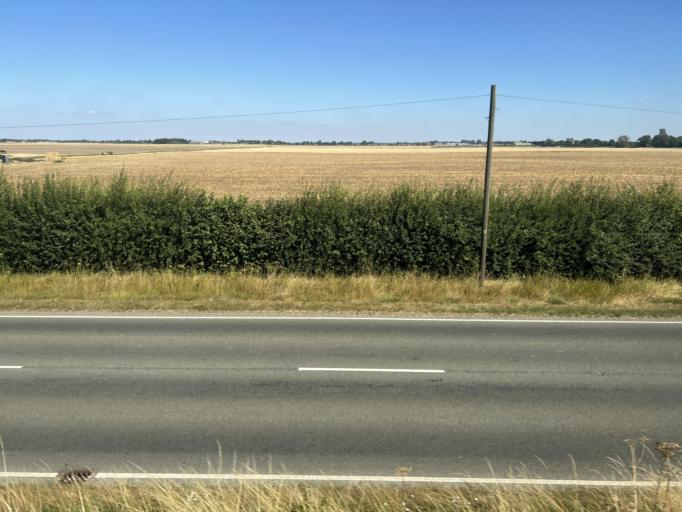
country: GB
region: England
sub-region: Lincolnshire
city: Kirton
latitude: 52.9737
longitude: -0.0824
